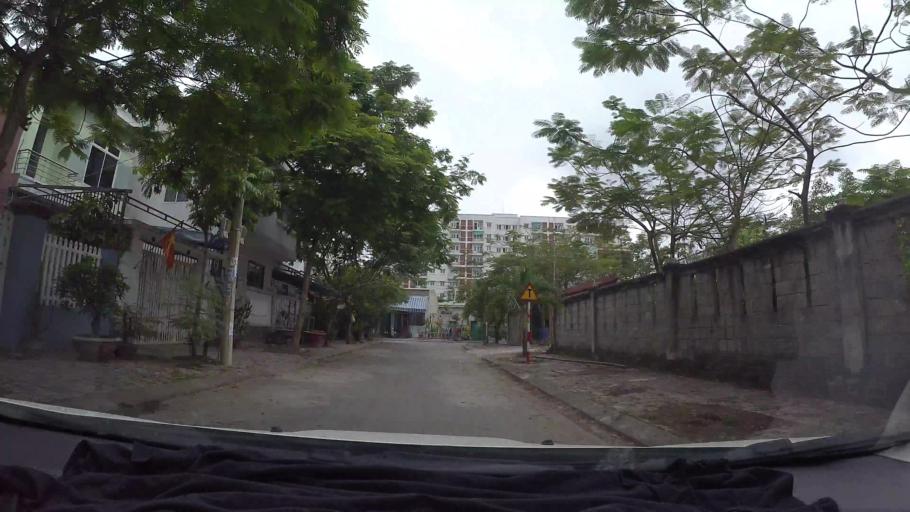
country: VN
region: Da Nang
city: Thanh Khe
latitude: 16.0462
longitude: 108.1741
